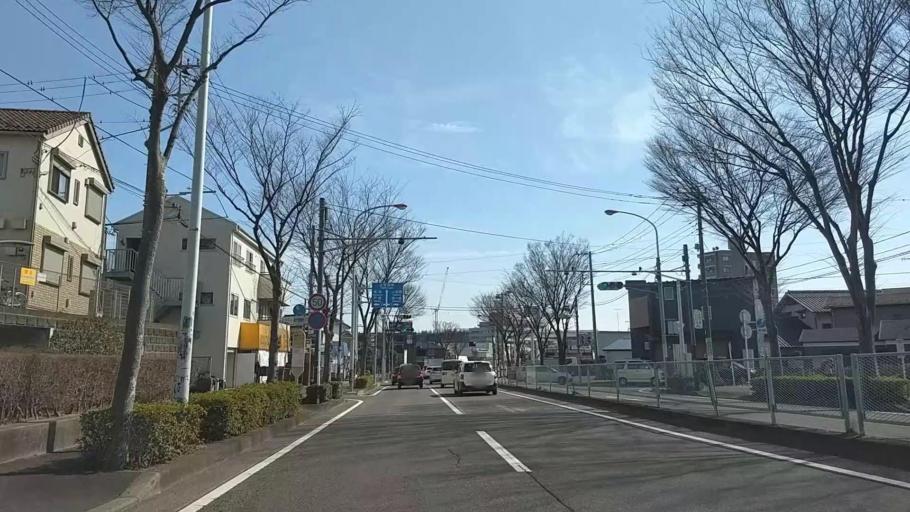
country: JP
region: Kanagawa
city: Fujisawa
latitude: 35.3469
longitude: 139.4479
